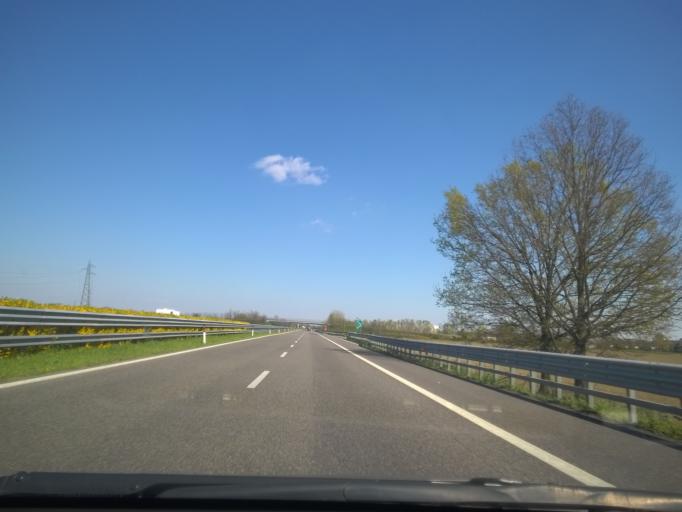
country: IT
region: Emilia-Romagna
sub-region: Provincia di Piacenza
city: Pontenure
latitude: 45.0448
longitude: 9.8166
